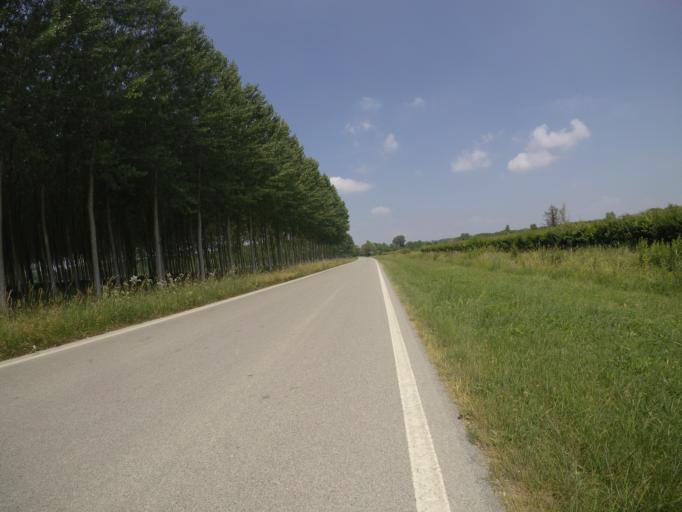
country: IT
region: Friuli Venezia Giulia
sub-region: Provincia di Udine
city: Rivignano
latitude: 45.8941
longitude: 13.0490
